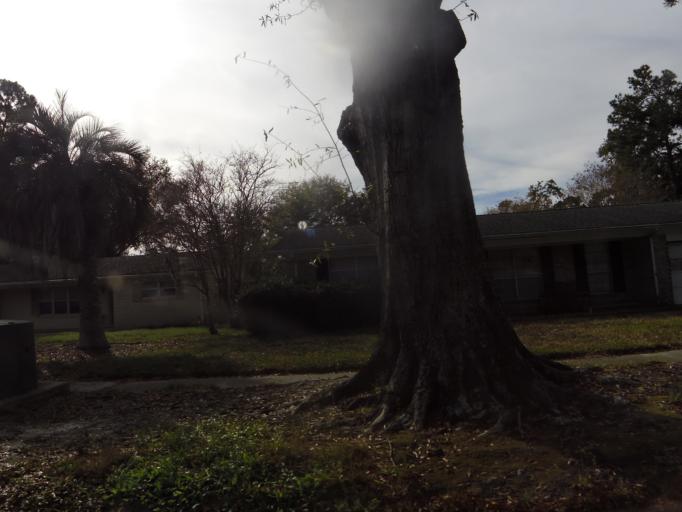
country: US
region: Florida
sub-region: Duval County
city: Jacksonville
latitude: 30.2269
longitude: -81.5942
